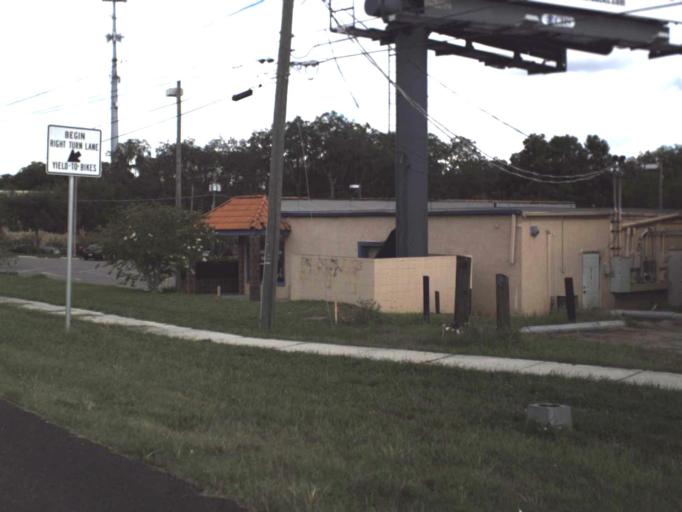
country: US
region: Florida
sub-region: Hillsborough County
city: Temple Terrace
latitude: 28.0545
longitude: -82.3990
